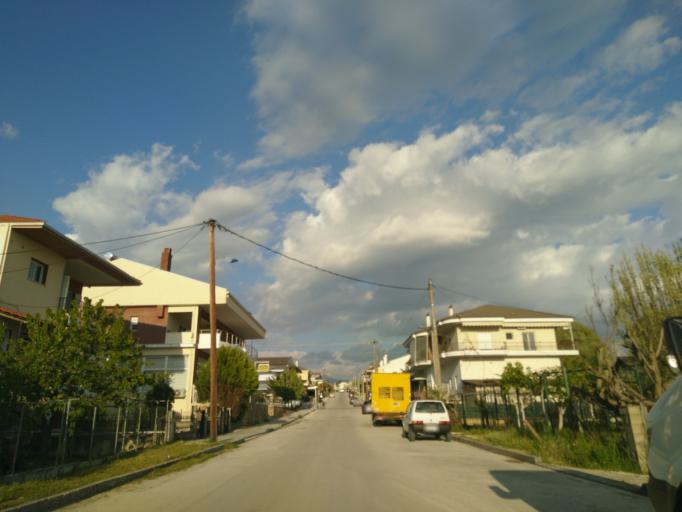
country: GR
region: Epirus
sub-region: Nomos Ioanninon
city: Anatoli
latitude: 39.6323
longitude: 20.8627
